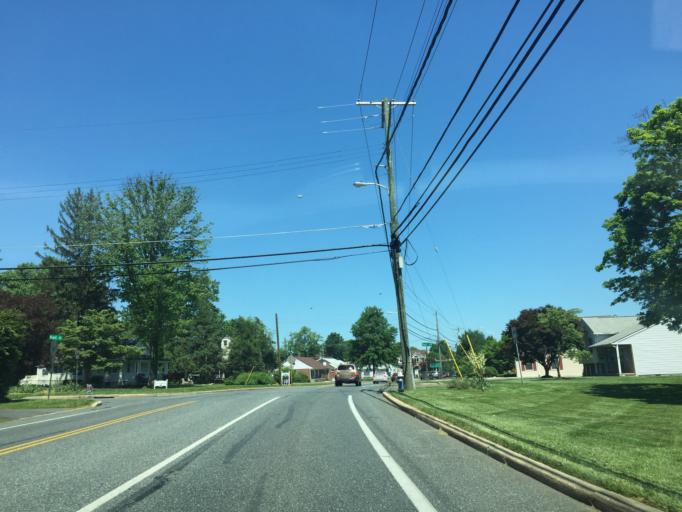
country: US
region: Maryland
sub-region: Harford County
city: North Bel Air
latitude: 39.5436
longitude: -76.3601
